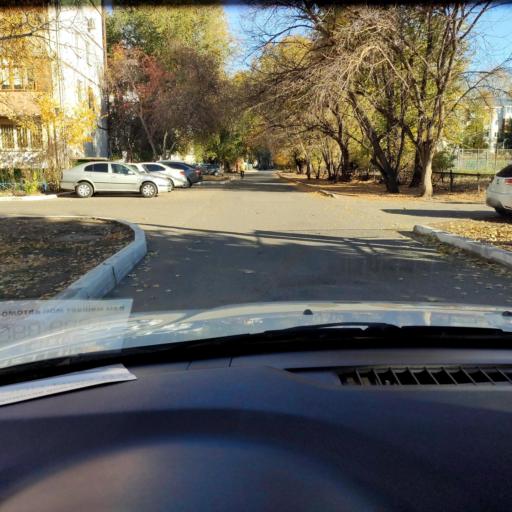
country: RU
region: Samara
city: Tol'yatti
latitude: 53.5130
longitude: 49.4247
